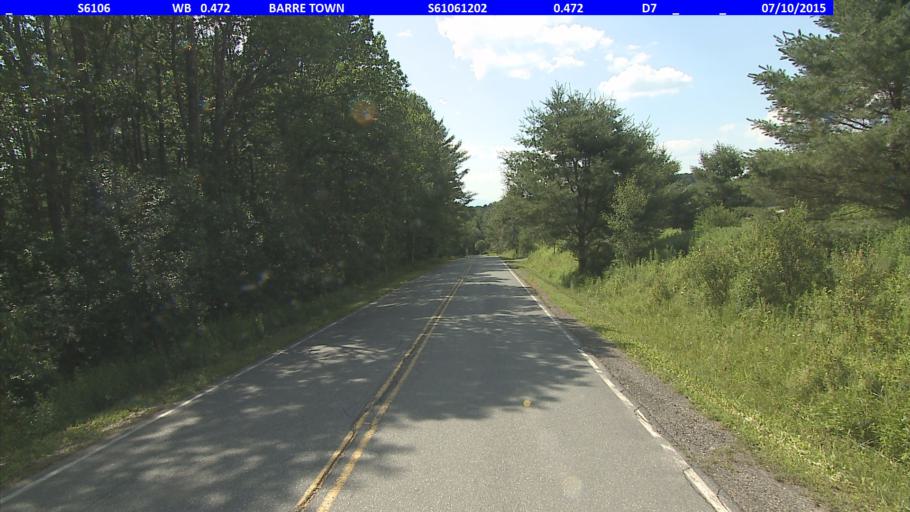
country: US
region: Vermont
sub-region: Washington County
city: Barre
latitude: 44.2194
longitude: -72.4735
